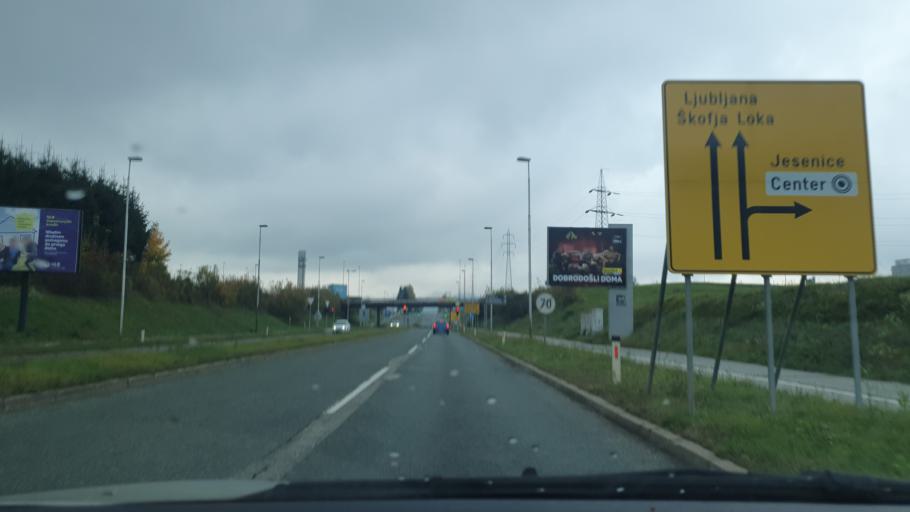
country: SI
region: Kranj
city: Kranj
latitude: 46.2275
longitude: 14.3585
